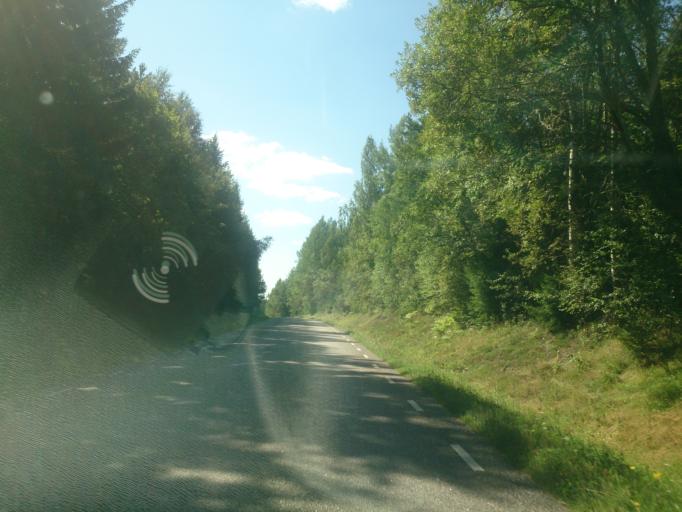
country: SE
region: OEstergoetland
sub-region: Atvidabergs Kommun
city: Atvidaberg
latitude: 58.2542
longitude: 16.0207
